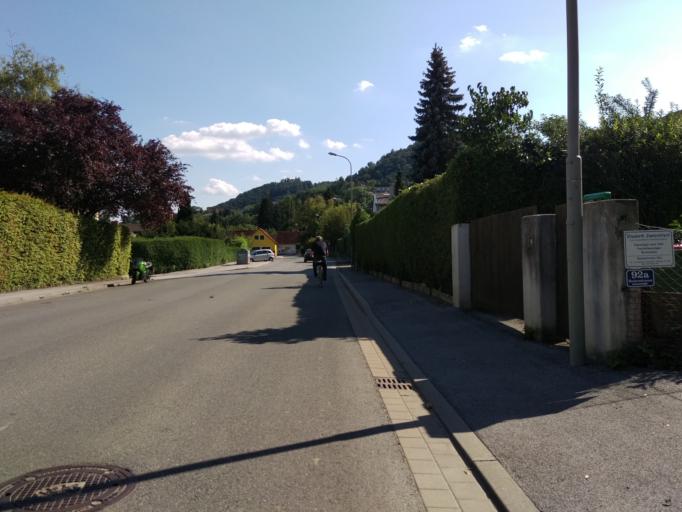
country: AT
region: Styria
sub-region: Graz Stadt
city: Wetzelsdorf
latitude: 47.0659
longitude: 15.3879
